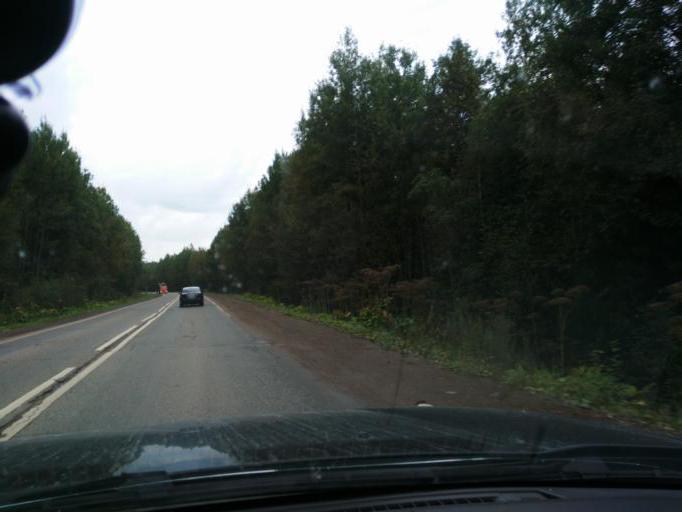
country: RU
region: Perm
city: Chernushka
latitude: 56.7007
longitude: 56.1831
